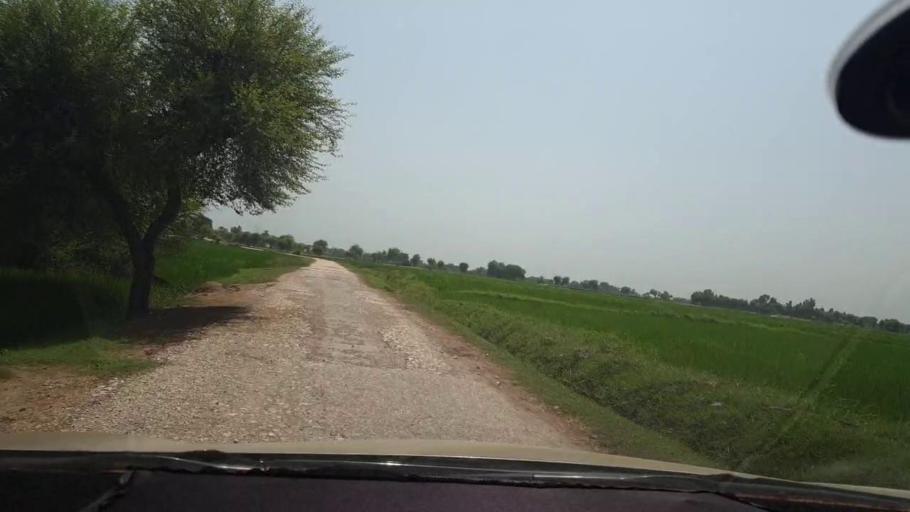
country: PK
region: Sindh
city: Kambar
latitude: 27.6417
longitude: 67.9325
